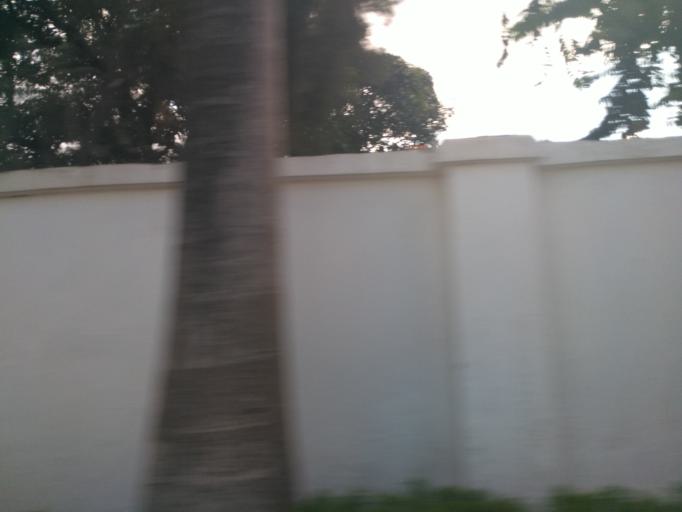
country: TZ
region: Dar es Salaam
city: Magomeni
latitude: -6.7735
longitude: 39.2587
